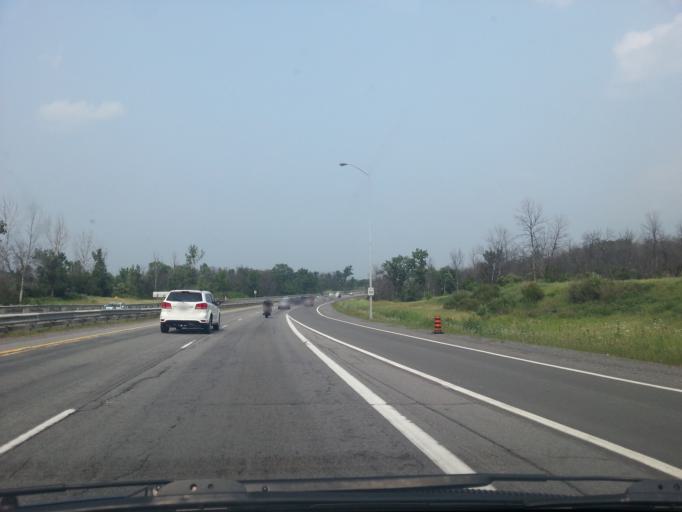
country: CA
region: Quebec
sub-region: Outaouais
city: Gatineau
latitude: 45.4547
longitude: -75.5810
